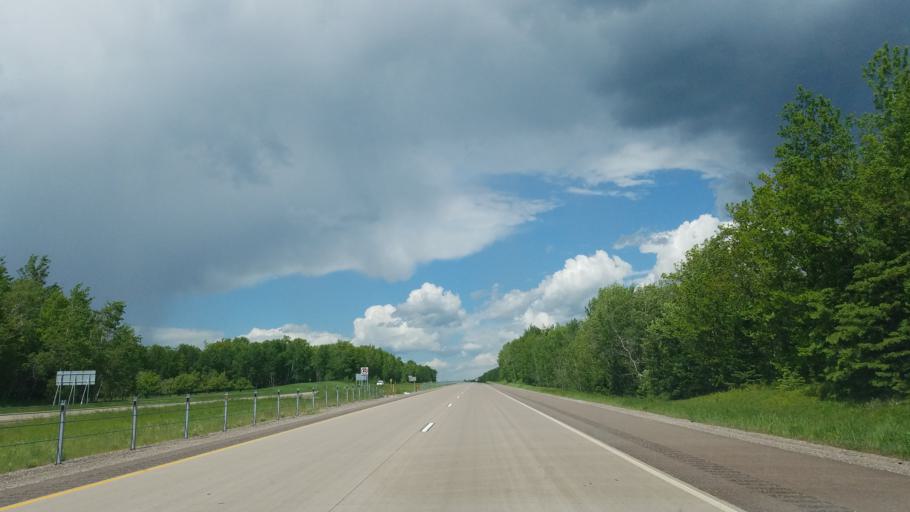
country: US
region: Minnesota
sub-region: Carlton County
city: Moose Lake
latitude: 46.4585
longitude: -92.7253
